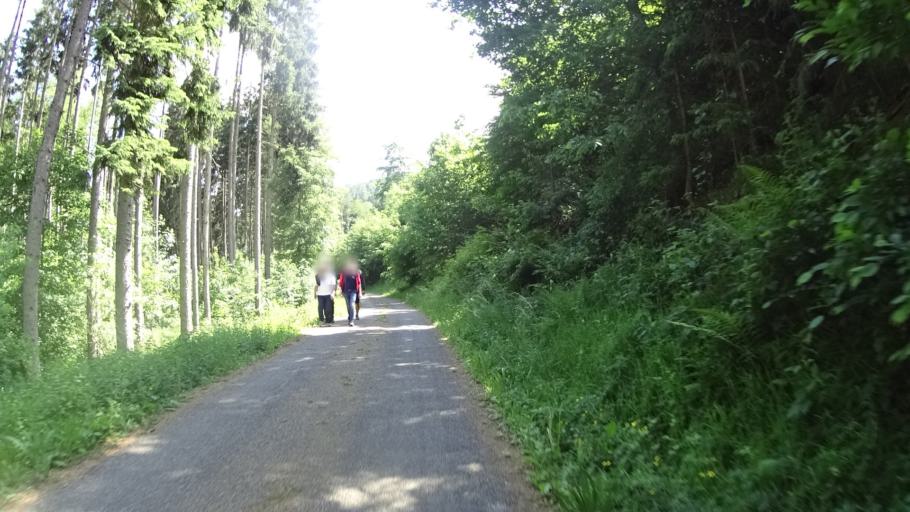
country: DE
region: Baden-Wuerttemberg
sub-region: Karlsruhe Region
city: Hopfingen
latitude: 49.6356
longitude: 9.4399
